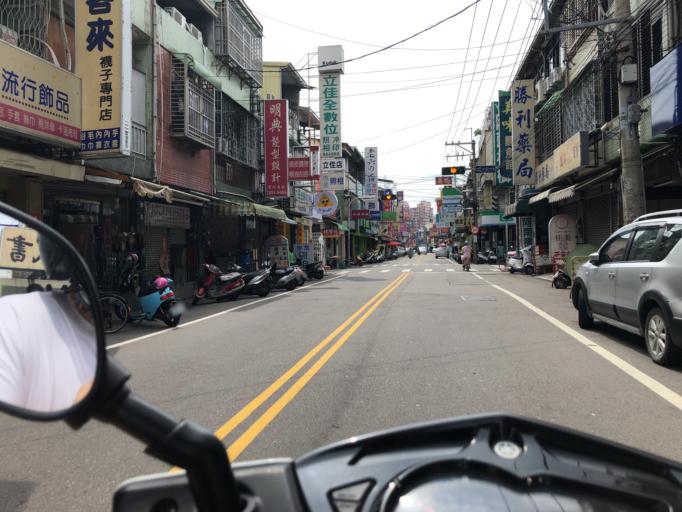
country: TW
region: Taiwan
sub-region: Taichung City
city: Taichung
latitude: 24.0898
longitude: 120.6984
